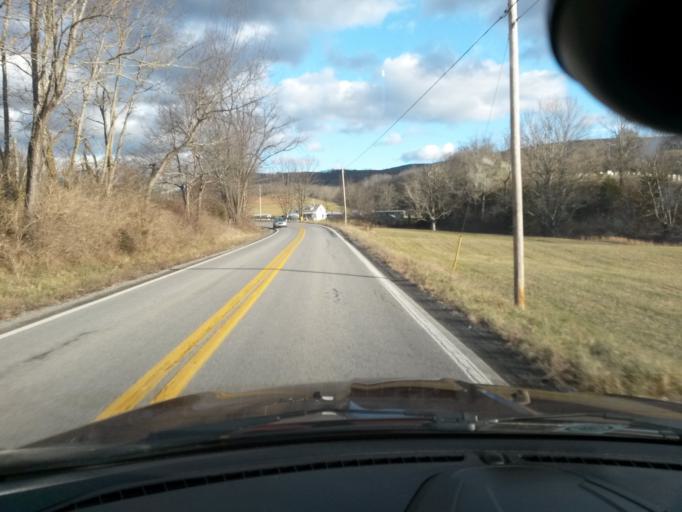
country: US
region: West Virginia
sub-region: Monroe County
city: Union
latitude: 37.4781
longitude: -80.6325
